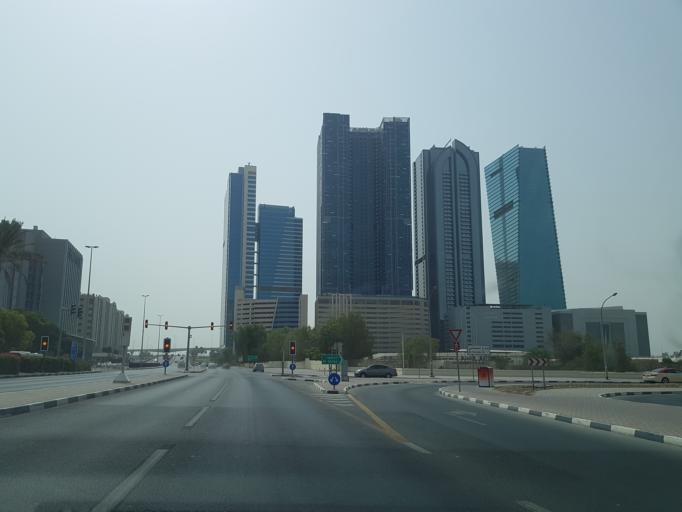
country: AE
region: Ash Shariqah
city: Sharjah
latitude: 25.2324
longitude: 55.2830
